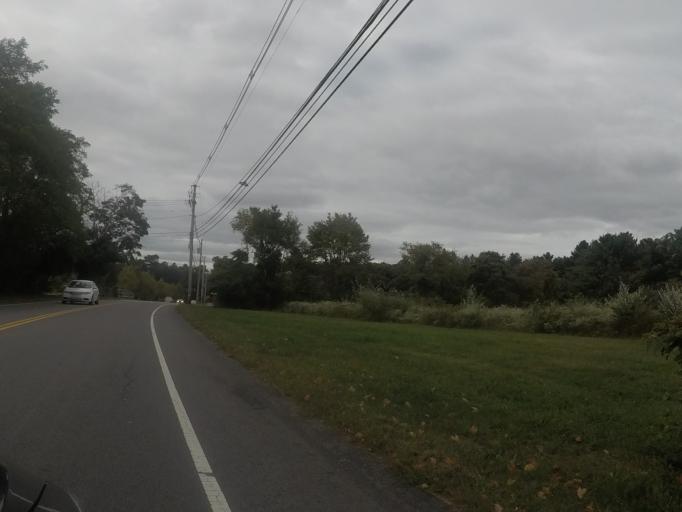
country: US
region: Massachusetts
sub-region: Bristol County
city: Smith Mills
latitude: 41.6752
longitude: -70.9883
